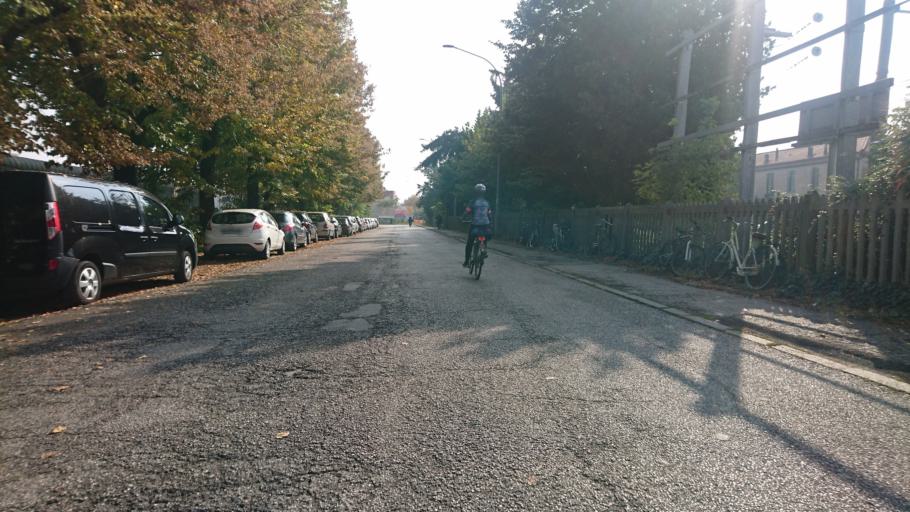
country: IT
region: Veneto
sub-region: Provincia di Rovigo
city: Rovigo
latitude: 45.0762
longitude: 11.7813
